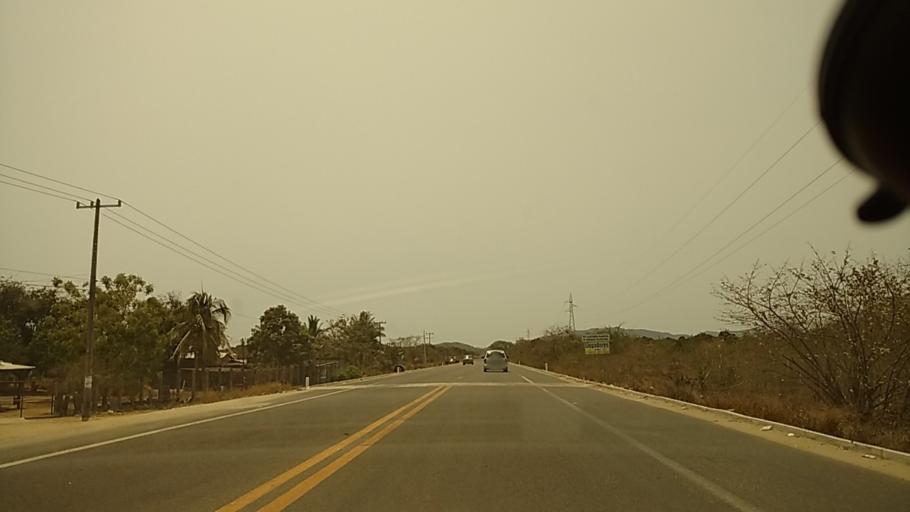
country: MX
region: Guerrero
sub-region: Tecpan de Galeana
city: Villa Rotaria
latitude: 17.2727
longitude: -100.9554
